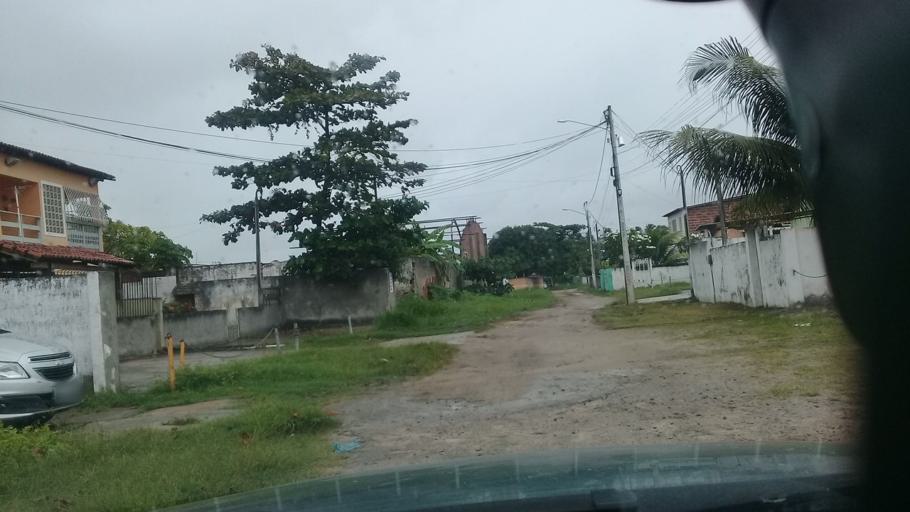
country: BR
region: Pernambuco
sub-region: Itamaraca
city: Itamaraca
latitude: -7.7558
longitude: -34.8268
